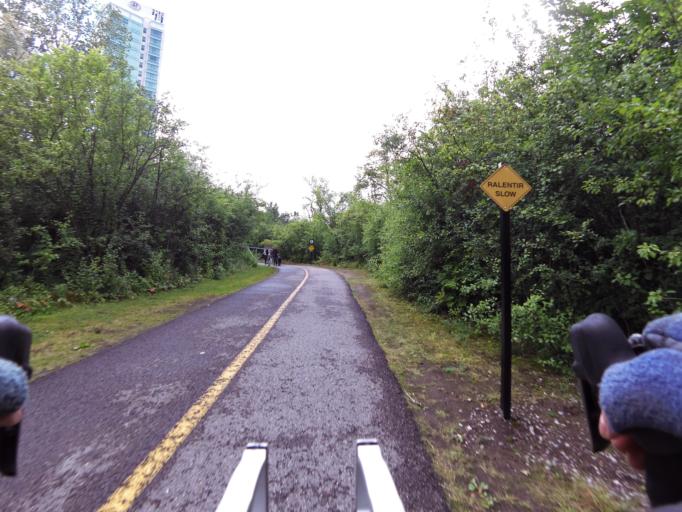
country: CA
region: Quebec
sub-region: Outaouais
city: Gatineau
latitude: 45.4472
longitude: -75.7217
